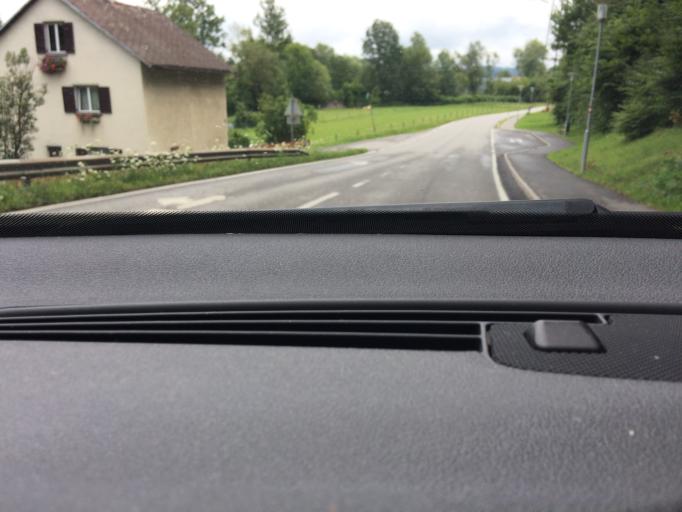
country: AT
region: Styria
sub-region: Politischer Bezirk Weiz
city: Gleisdorf
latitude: 47.0988
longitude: 15.6967
